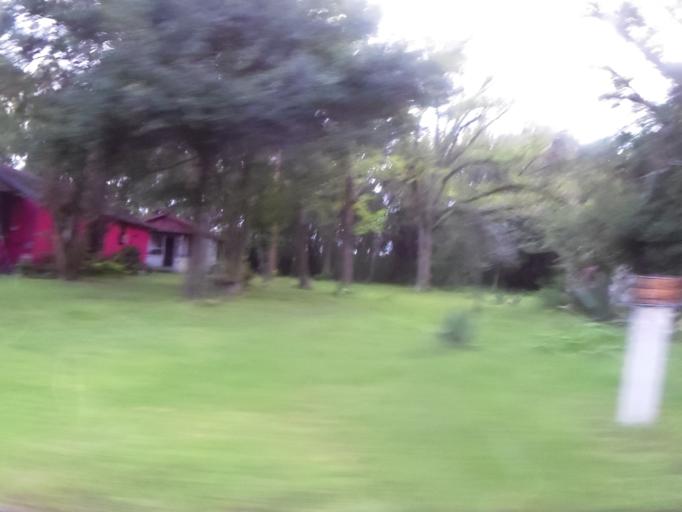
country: US
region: Florida
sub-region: Duval County
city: Jacksonville
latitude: 30.3514
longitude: -81.7053
